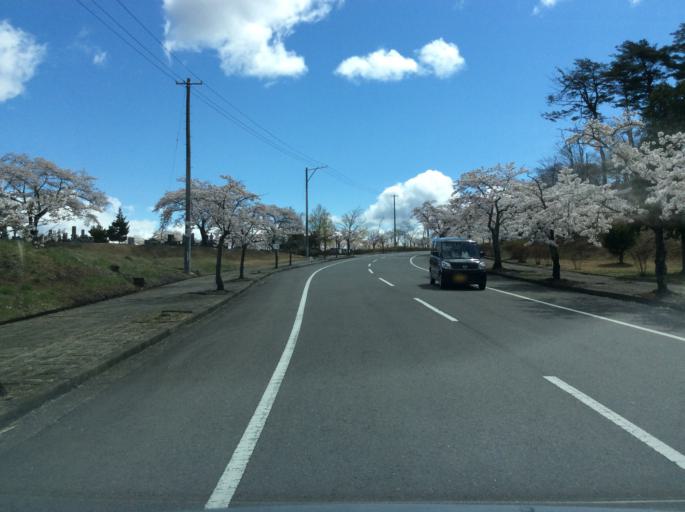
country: JP
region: Fukushima
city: Koriyama
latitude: 37.3478
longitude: 140.4351
